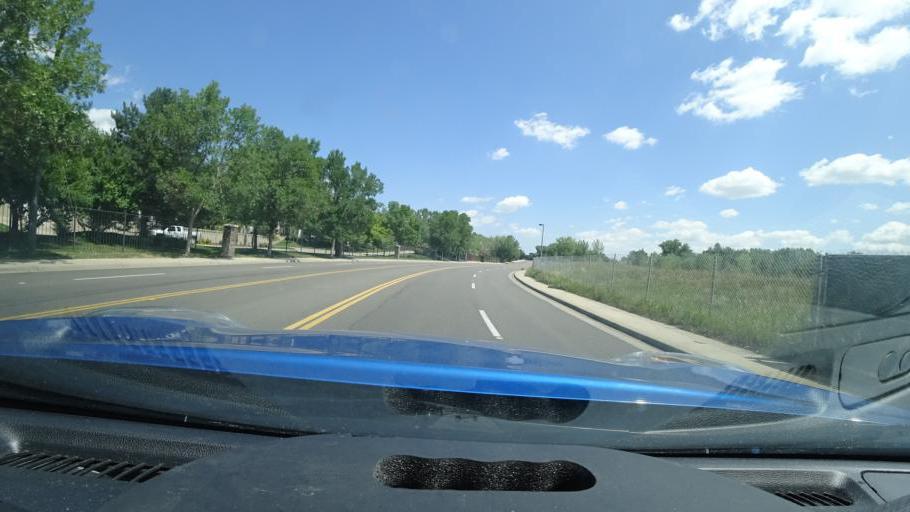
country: US
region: Colorado
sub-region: Arapahoe County
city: Glendale
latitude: 39.7017
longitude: -104.8924
